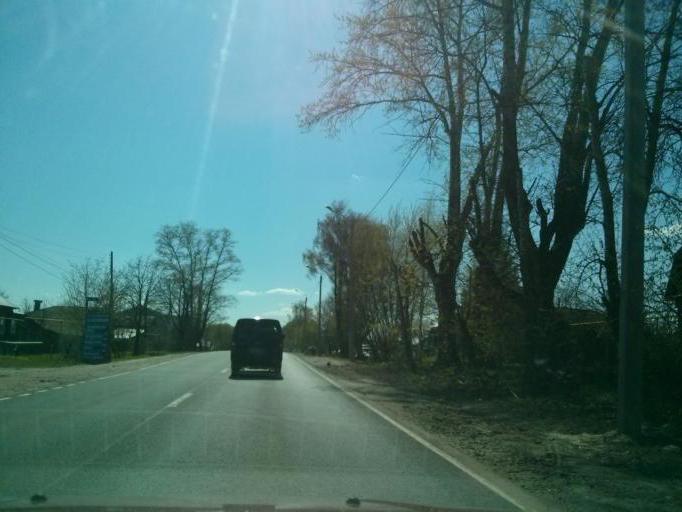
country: RU
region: Nizjnij Novgorod
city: Vorsma
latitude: 56.0358
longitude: 43.3677
